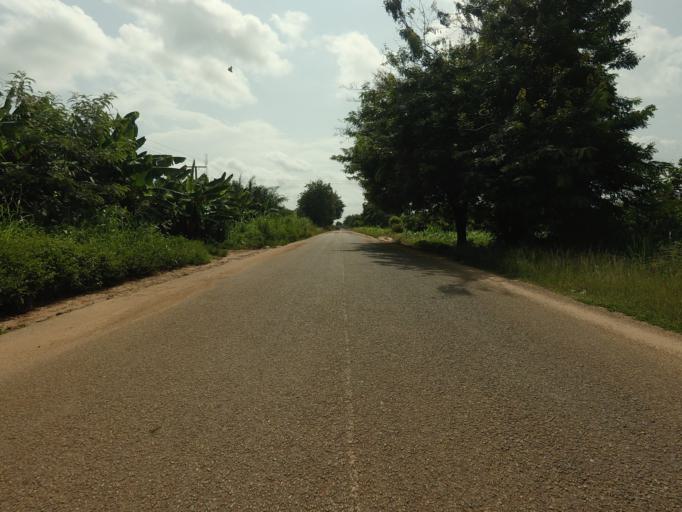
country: TG
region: Maritime
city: Lome
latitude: 6.2655
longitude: 0.9525
